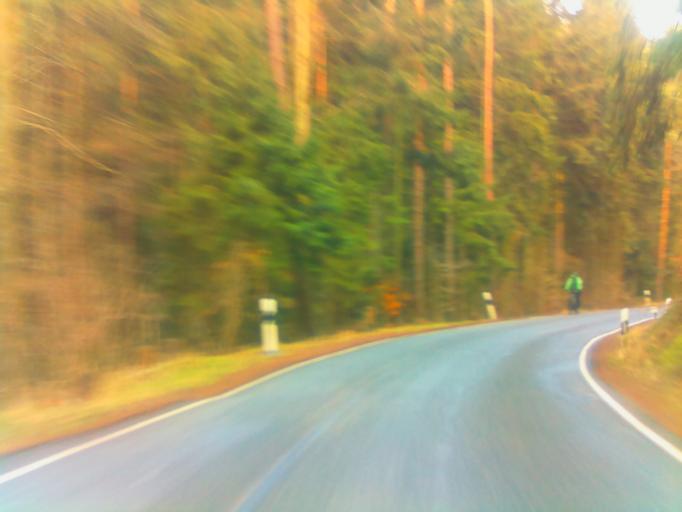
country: DE
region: Thuringia
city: Saalfeld
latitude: 50.6784
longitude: 11.3973
